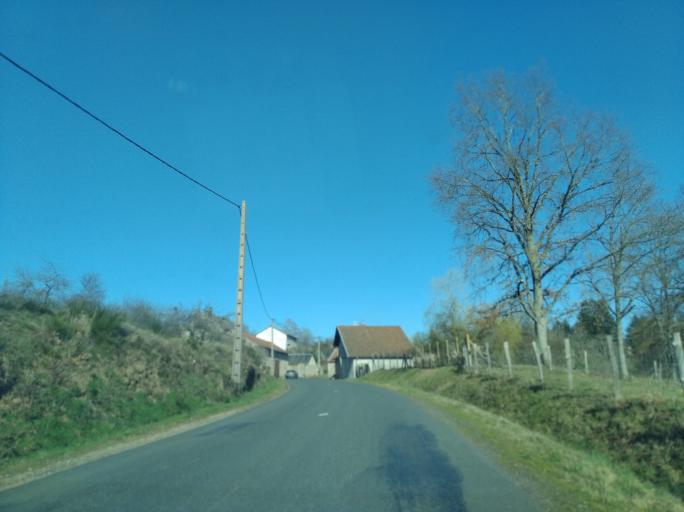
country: FR
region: Auvergne
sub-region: Departement de l'Allier
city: Le Mayet-de-Montagne
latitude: 46.1001
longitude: 3.7121
